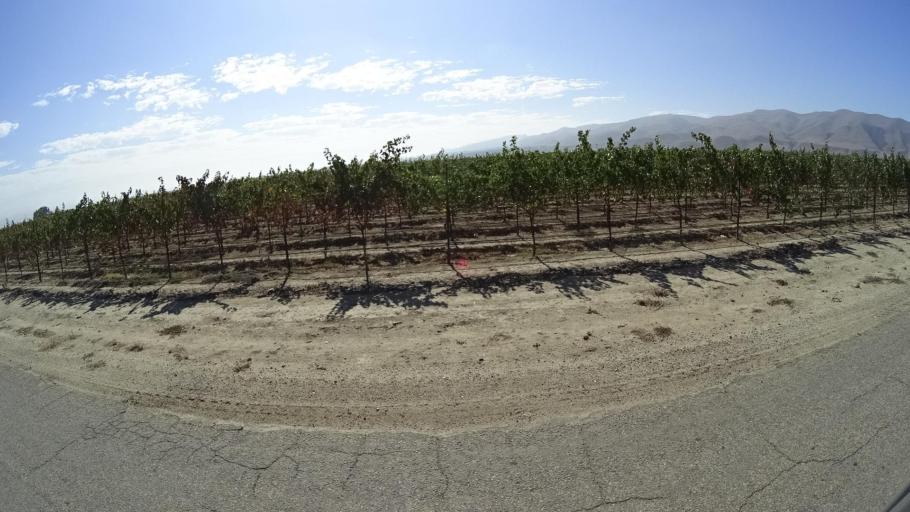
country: US
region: California
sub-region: Monterey County
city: Greenfield
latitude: 36.3070
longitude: -121.2712
